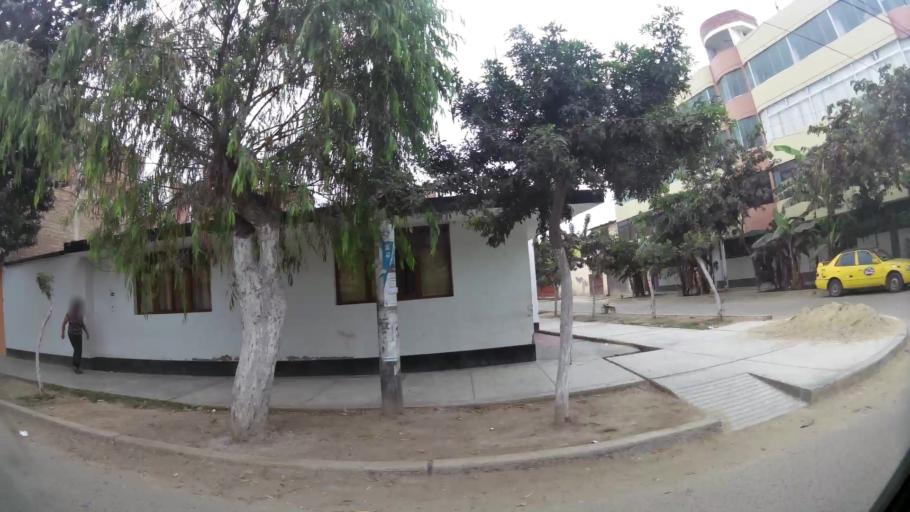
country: PE
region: La Libertad
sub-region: Provincia de Trujillo
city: Buenos Aires
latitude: -8.1384
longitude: -79.0462
